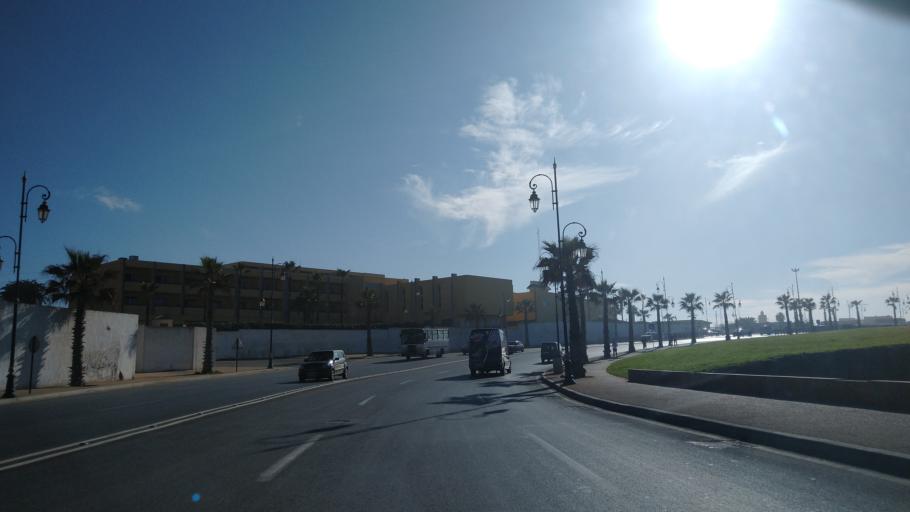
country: MA
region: Rabat-Sale-Zemmour-Zaer
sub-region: Rabat
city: Rabat
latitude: 34.0197
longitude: -6.8563
